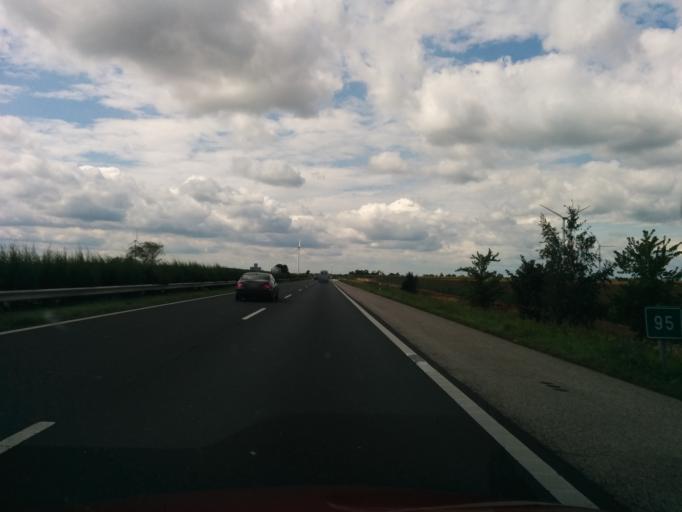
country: HU
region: Komarom-Esztergom
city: Babolna
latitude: 47.6799
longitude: 17.9597
